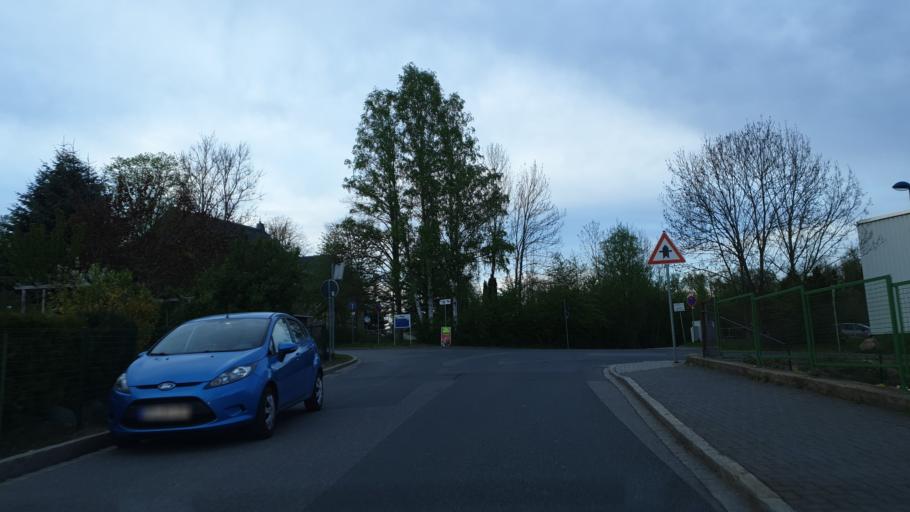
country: DE
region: Saxony
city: Oelsnitz
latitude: 50.7315
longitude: 12.7028
